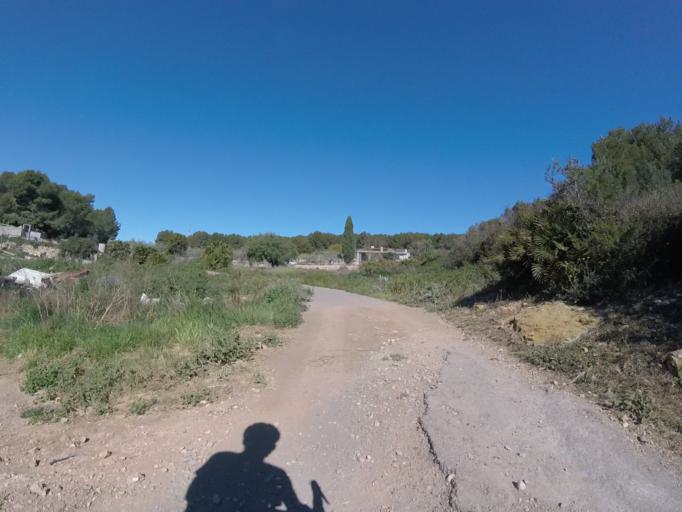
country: ES
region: Valencia
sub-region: Provincia de Castello
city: Benicassim
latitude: 40.0815
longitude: 0.0873
